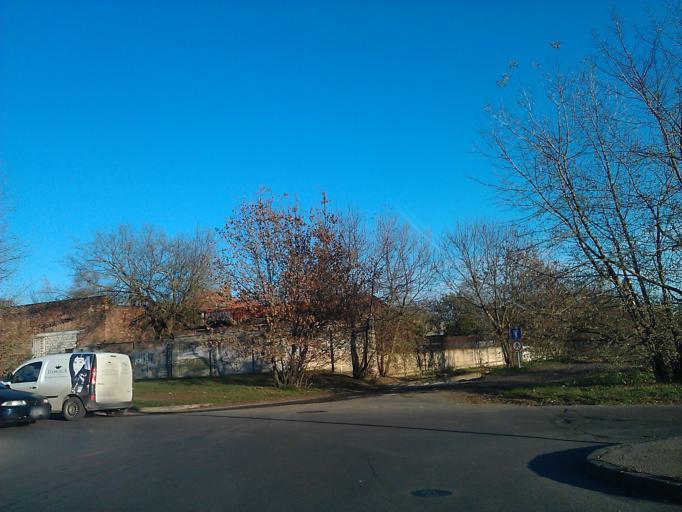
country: LV
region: Riga
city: Riga
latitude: 56.9389
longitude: 24.1339
